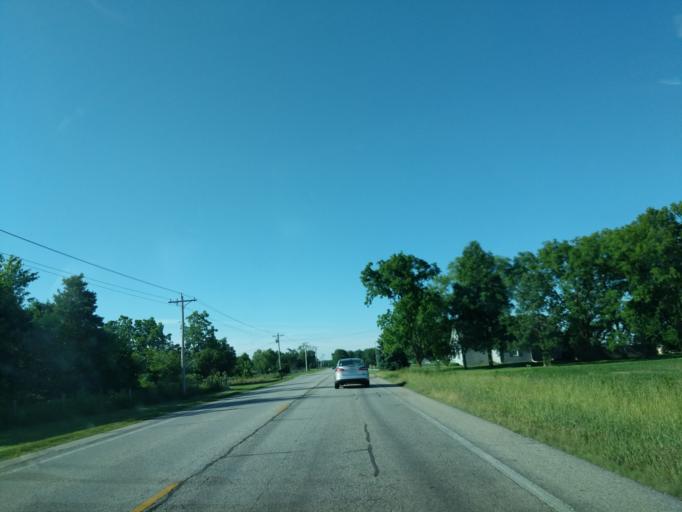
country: US
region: Indiana
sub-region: Shelby County
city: Shelbyville
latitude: 39.5827
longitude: -85.7765
